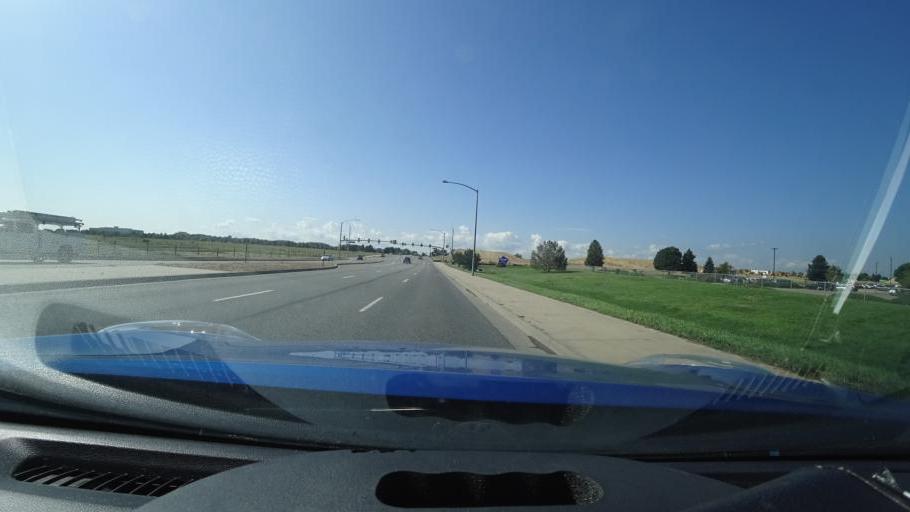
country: US
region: Colorado
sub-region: Adams County
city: Aurora
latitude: 39.7108
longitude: -104.7913
